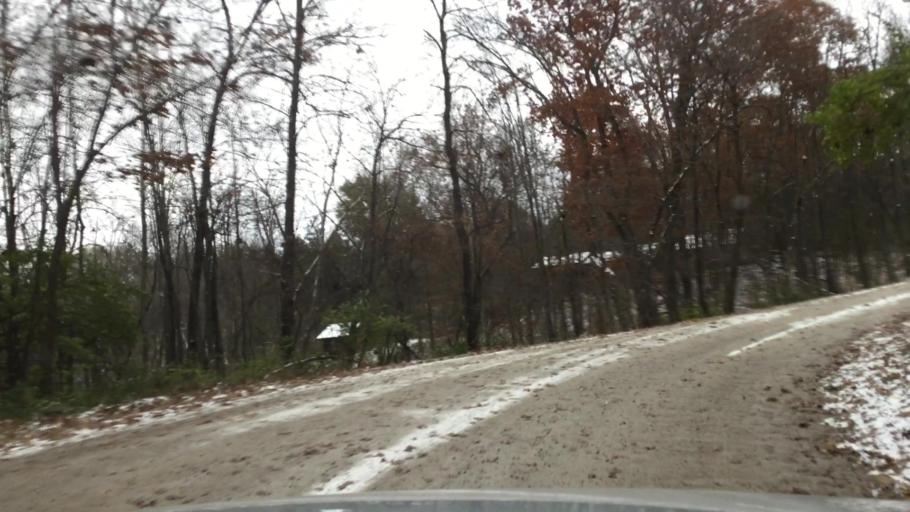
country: US
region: Michigan
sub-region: Livingston County
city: Brighton
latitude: 42.5401
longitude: -83.7115
